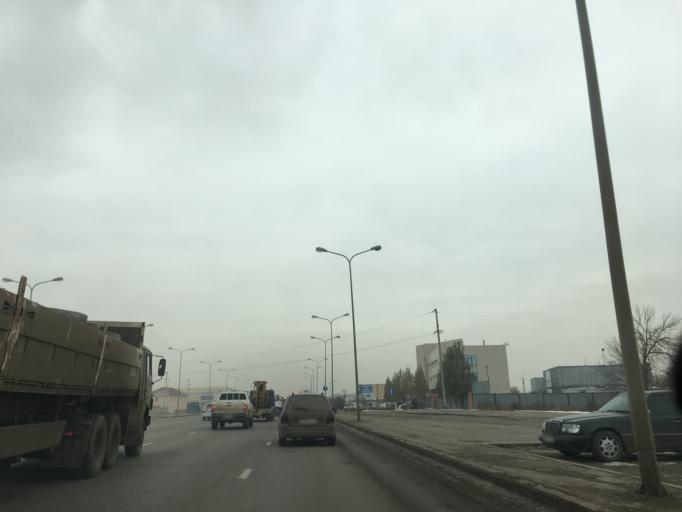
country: KZ
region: Astana Qalasy
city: Astana
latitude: 51.1777
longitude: 71.4715
